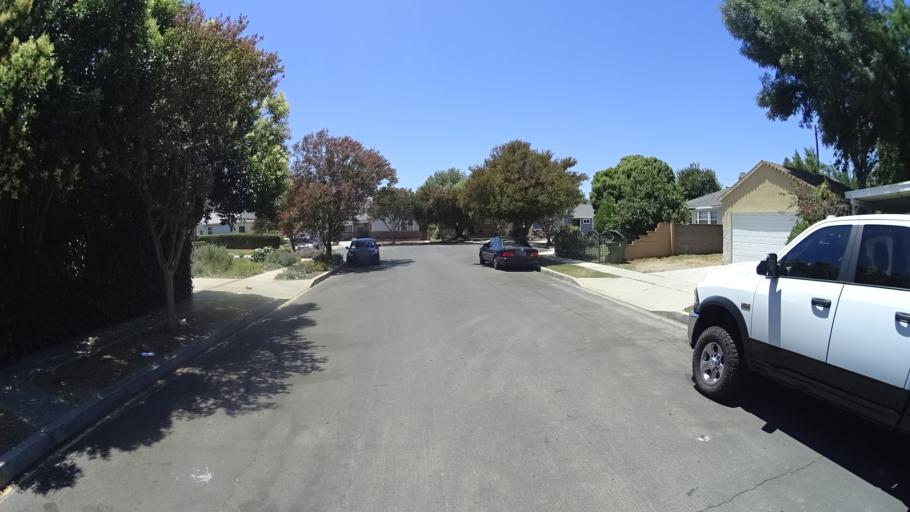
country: US
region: California
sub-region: Los Angeles County
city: Northridge
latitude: 34.1912
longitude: -118.5287
